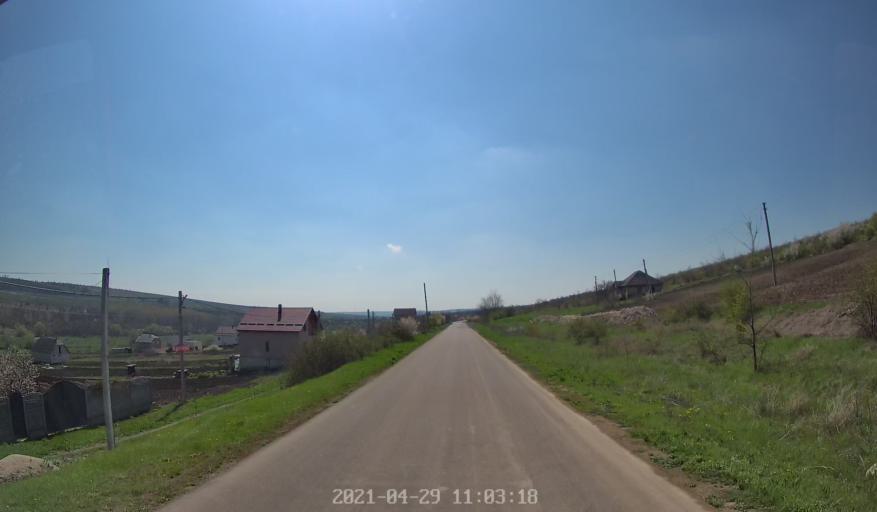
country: MD
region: Chisinau
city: Ciorescu
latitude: 47.1570
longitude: 28.9566
